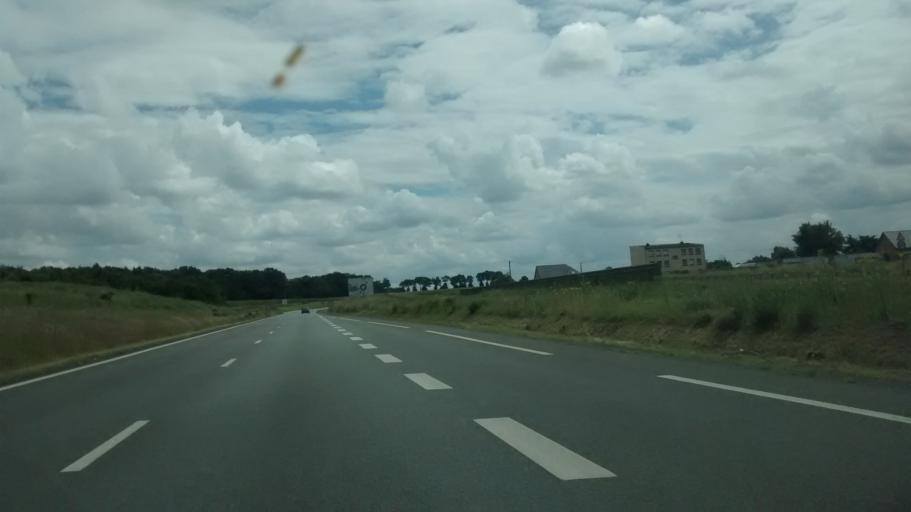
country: FR
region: Brittany
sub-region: Departement d'Ille-et-Vilaine
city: Saint-Jacques-de-la-Lande
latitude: 48.0798
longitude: -1.6963
